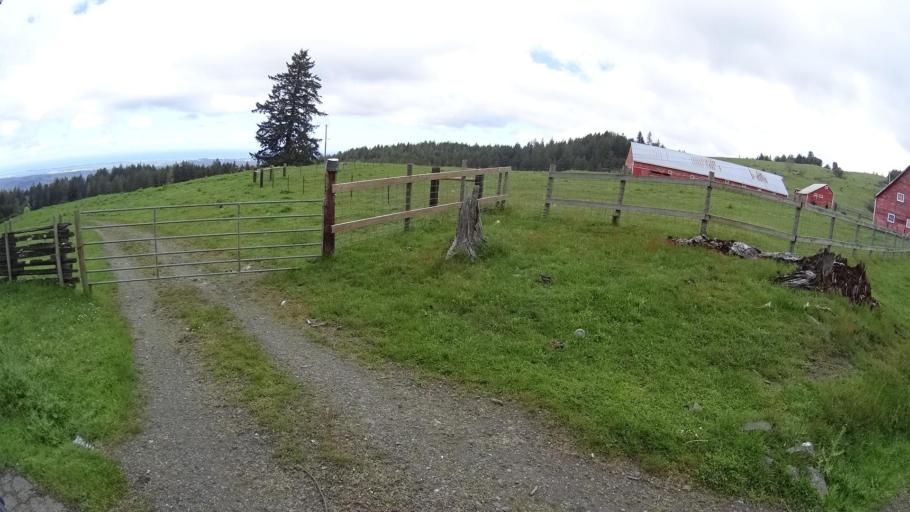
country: US
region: California
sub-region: Humboldt County
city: Blue Lake
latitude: 40.9101
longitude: -123.9636
